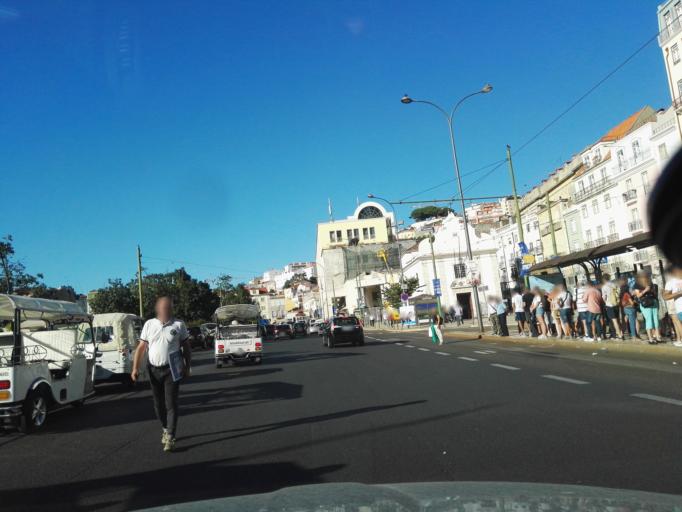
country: PT
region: Lisbon
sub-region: Lisbon
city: Lisbon
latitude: 38.7153
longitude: -9.1362
